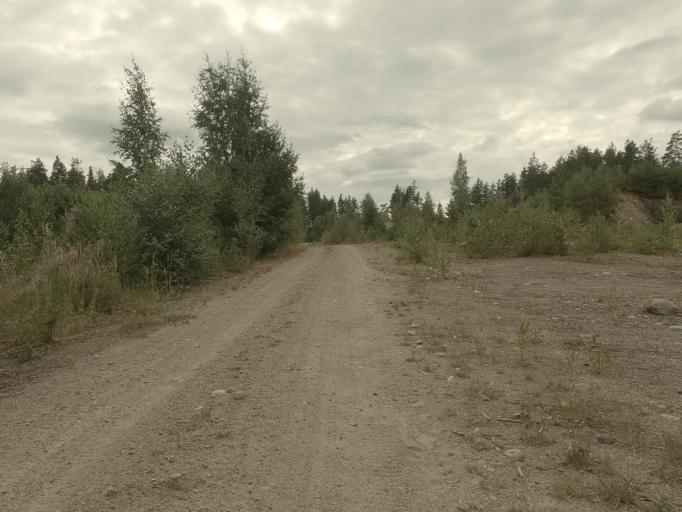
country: RU
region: Leningrad
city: Kamennogorsk
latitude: 61.0034
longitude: 29.1822
